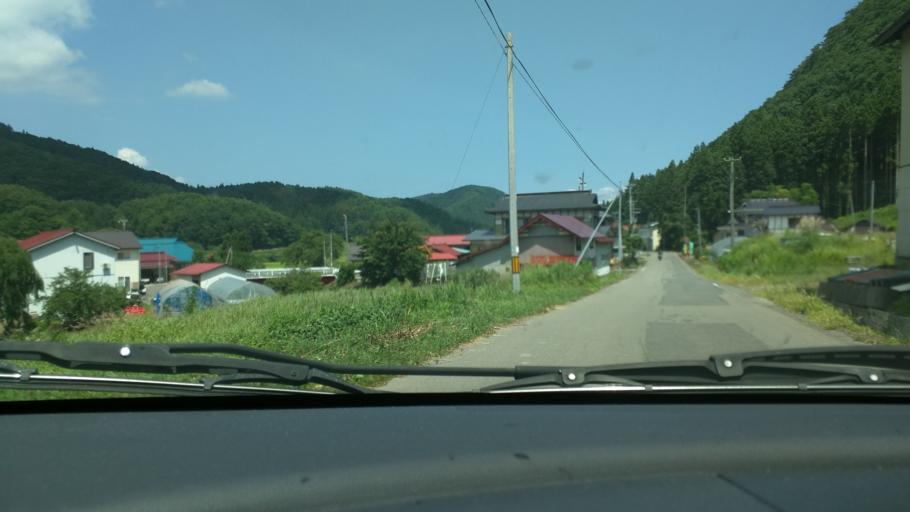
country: JP
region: Fukushima
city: Inawashiro
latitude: 37.3806
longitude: 140.0669
